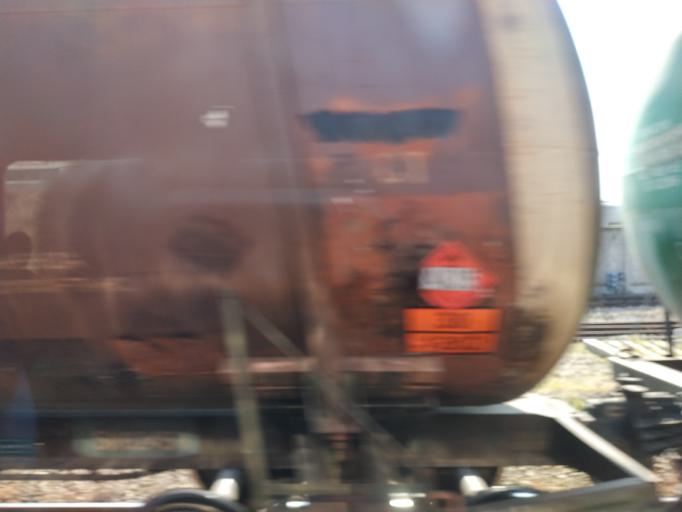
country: RU
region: Volgograd
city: Volgograd
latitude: 48.7187
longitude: 44.5240
